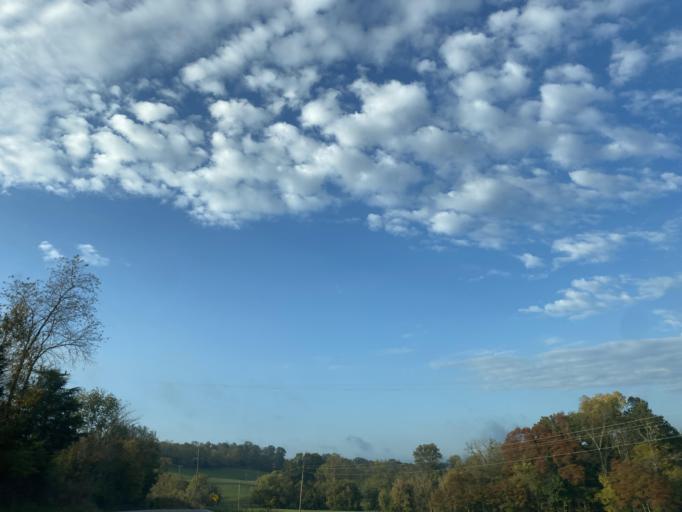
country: US
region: Kentucky
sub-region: Pendleton County
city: Falmouth
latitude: 38.7732
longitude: -84.3369
